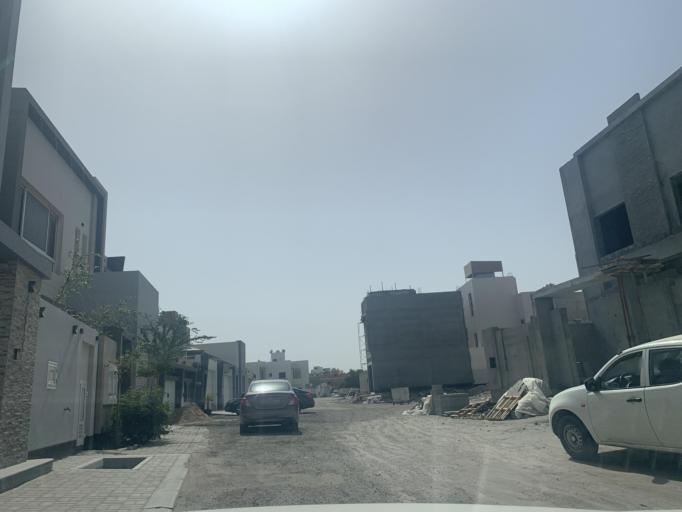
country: BH
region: Northern
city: Sitrah
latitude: 26.1691
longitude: 50.6290
